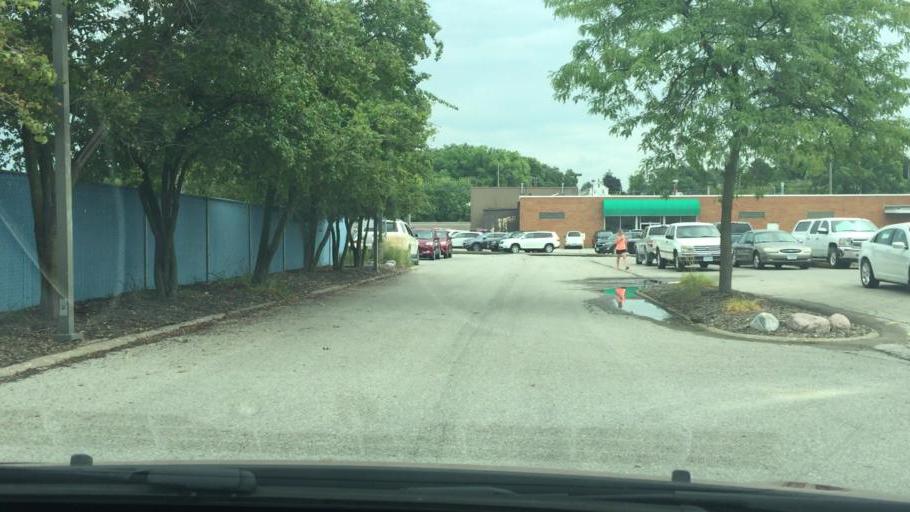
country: US
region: Iowa
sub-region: Muscatine County
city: Muscatine
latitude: 41.4254
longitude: -91.0394
